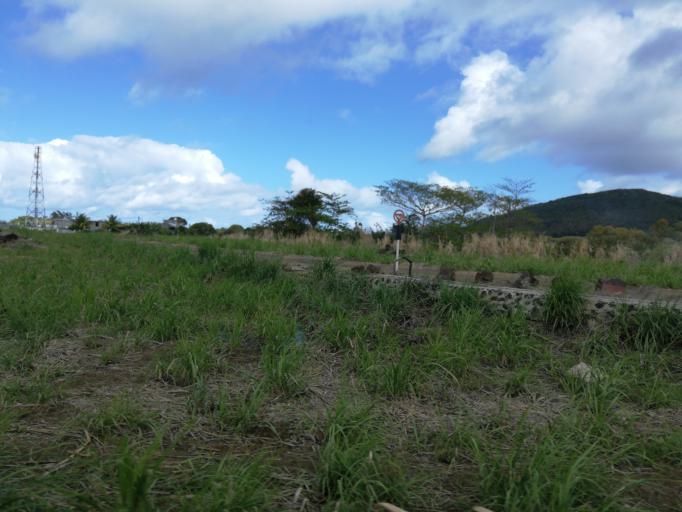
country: MU
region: Flacq
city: Grande Riviere Sud Est
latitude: -20.2736
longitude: 57.7692
